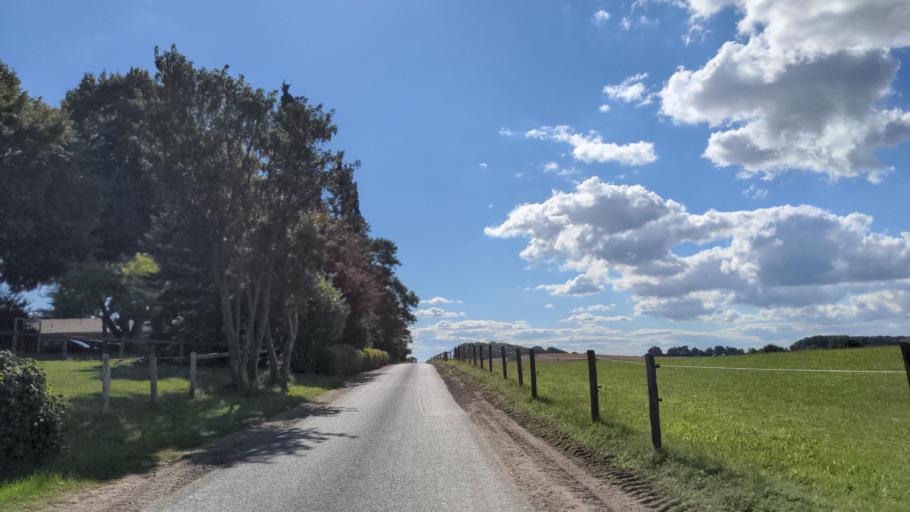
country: DE
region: Schleswig-Holstein
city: Kasseedorf
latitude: 54.1332
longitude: 10.7224
